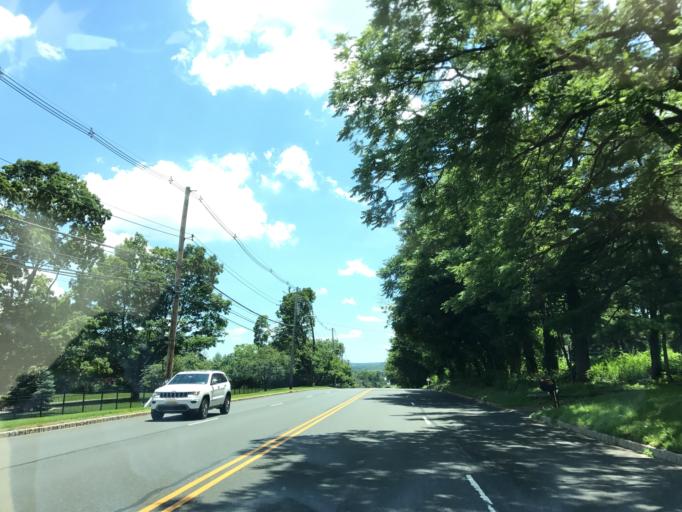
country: US
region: New Jersey
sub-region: Morris County
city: Madison
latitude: 40.7876
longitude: -74.4332
